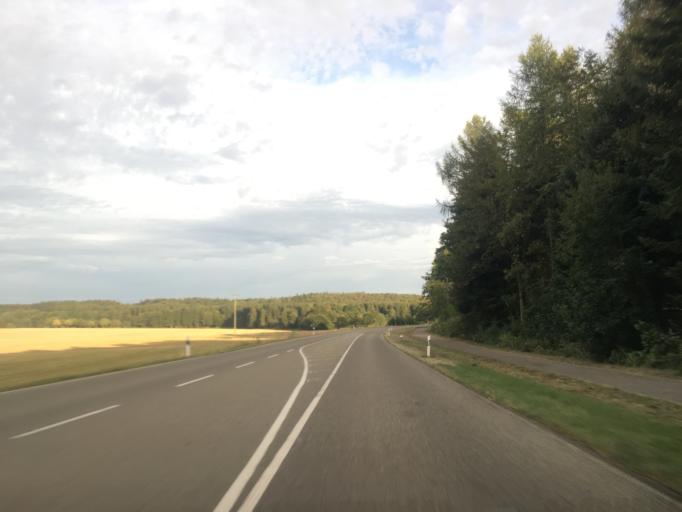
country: DE
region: Baden-Wuerttemberg
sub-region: Tuebingen Region
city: Sankt Johann
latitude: 48.4842
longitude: 9.3252
